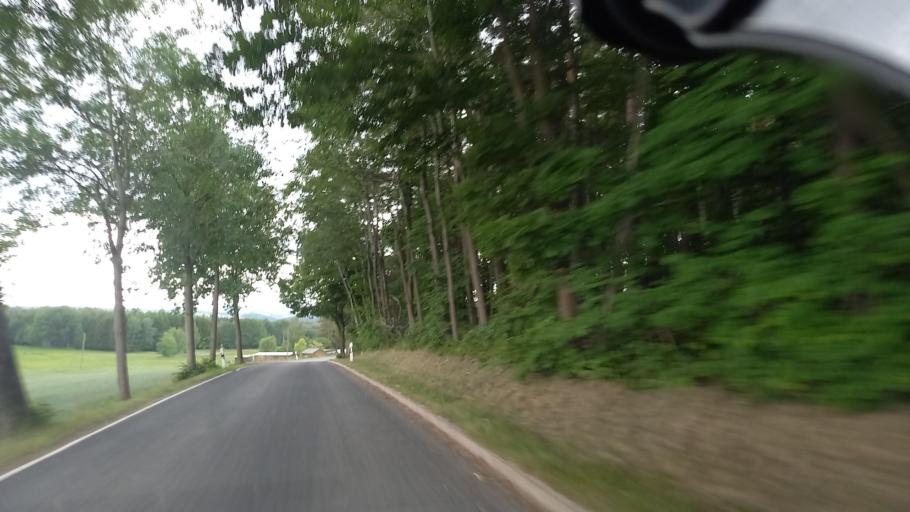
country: DE
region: Saxony
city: Waldkirchen
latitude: 50.5842
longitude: 12.4237
